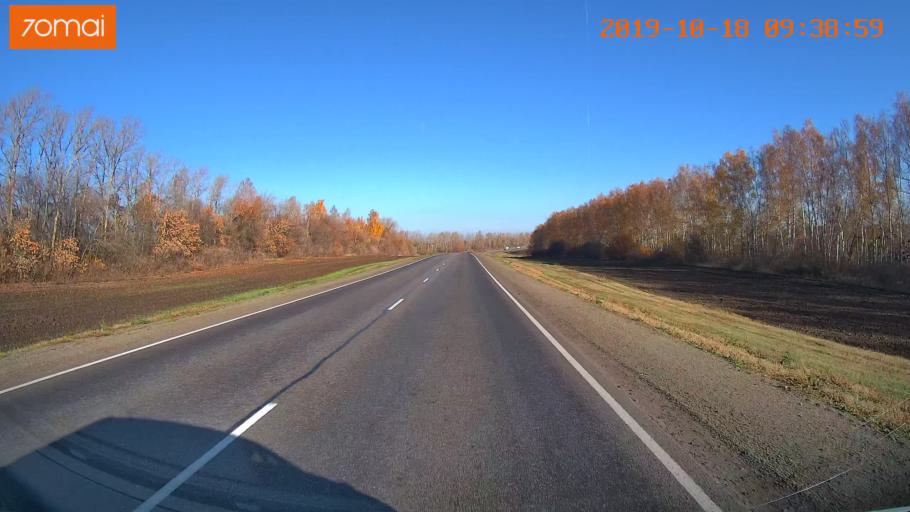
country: RU
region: Tula
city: Yefremov
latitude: 53.2463
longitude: 38.1348
